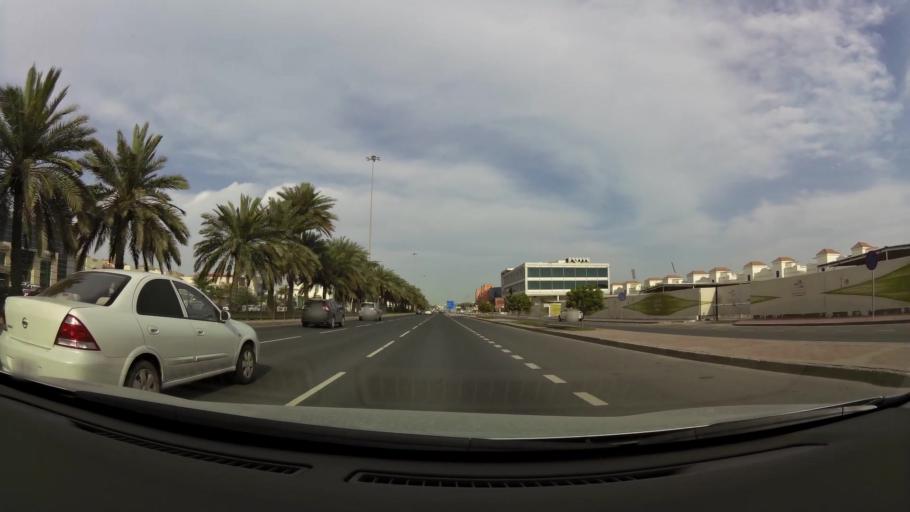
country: QA
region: Baladiyat ad Dawhah
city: Doha
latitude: 25.2542
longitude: 51.5288
